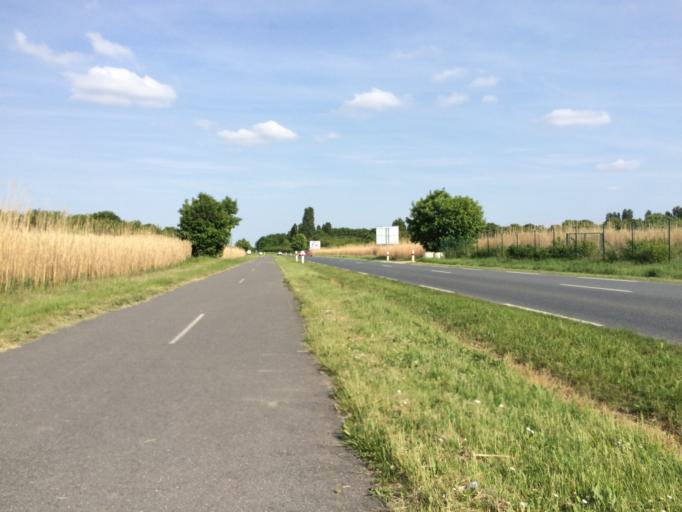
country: FR
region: Ile-de-France
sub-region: Departement de l'Essonne
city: Morangis
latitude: 48.7142
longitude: 2.3372
